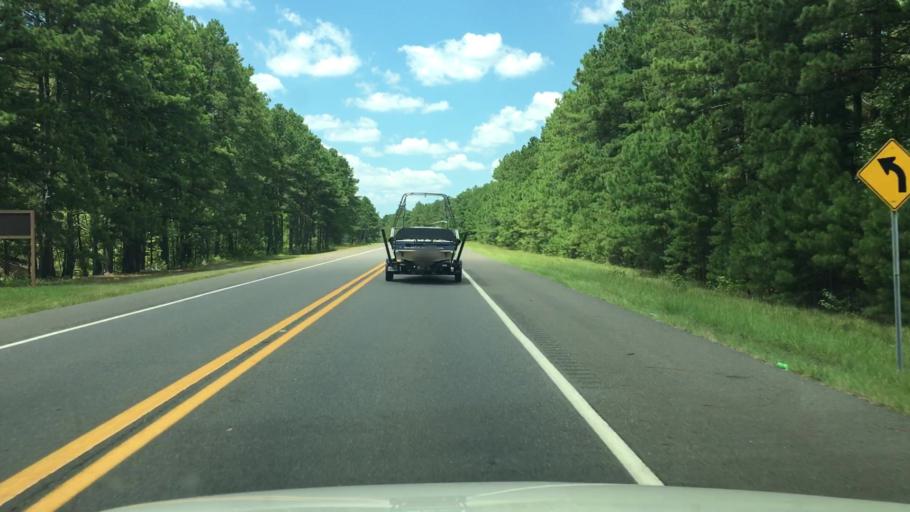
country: US
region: Arkansas
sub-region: Clark County
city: Arkadelphia
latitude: 34.2221
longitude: -93.0871
